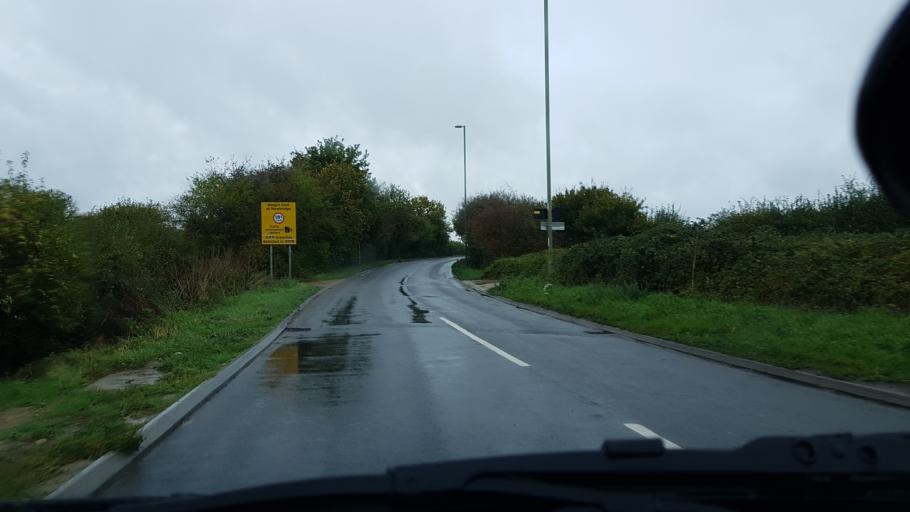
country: GB
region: England
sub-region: Oxfordshire
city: Frilford
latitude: 51.6856
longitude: -1.4127
